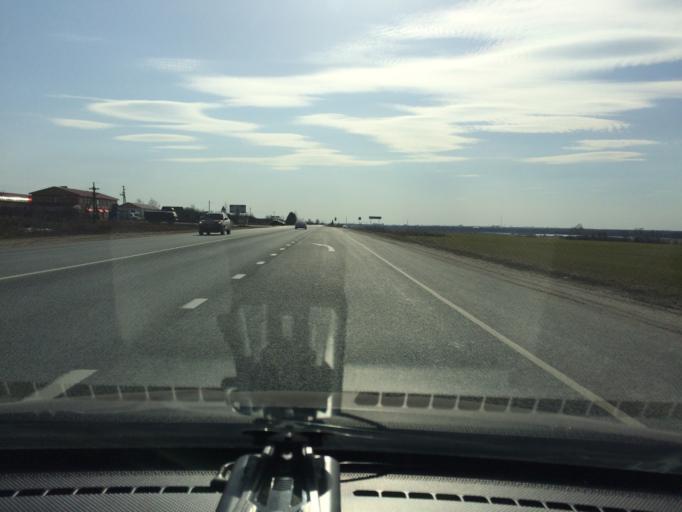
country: RU
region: Mariy-El
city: Yoshkar-Ola
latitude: 56.6675
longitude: 47.9945
